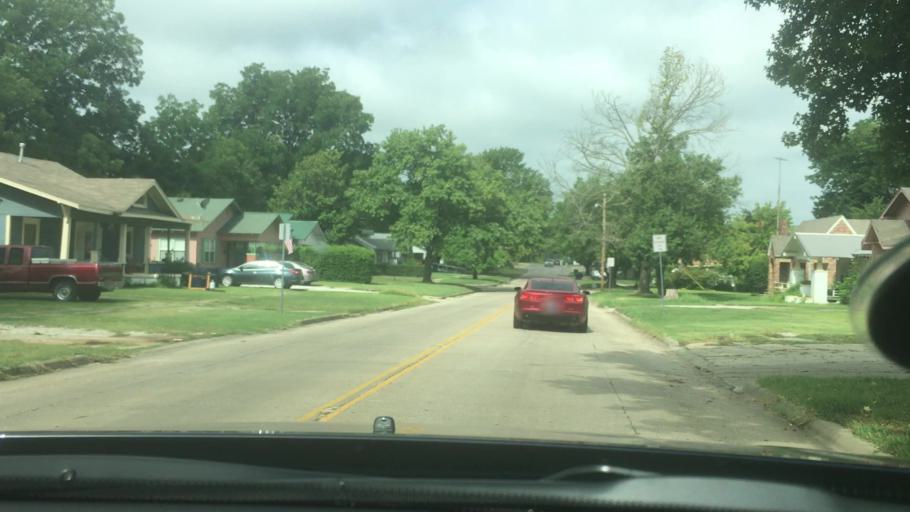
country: US
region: Oklahoma
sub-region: Pontotoc County
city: Ada
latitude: 34.7713
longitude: -96.6673
